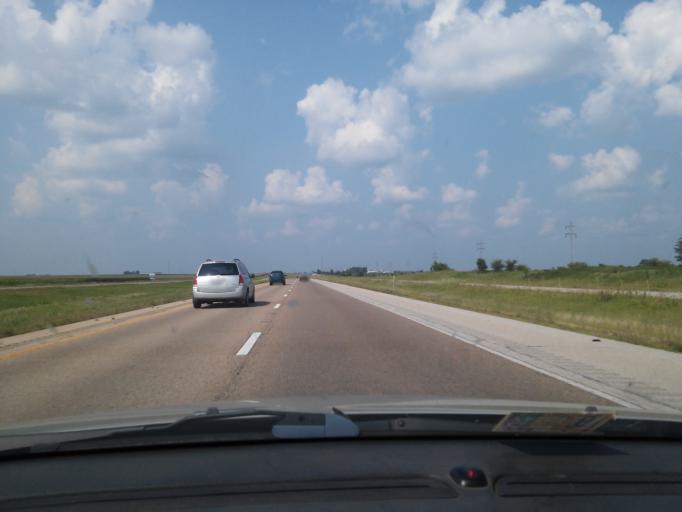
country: US
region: Illinois
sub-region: McLean County
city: Chenoa
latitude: 40.7060
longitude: -88.7457
